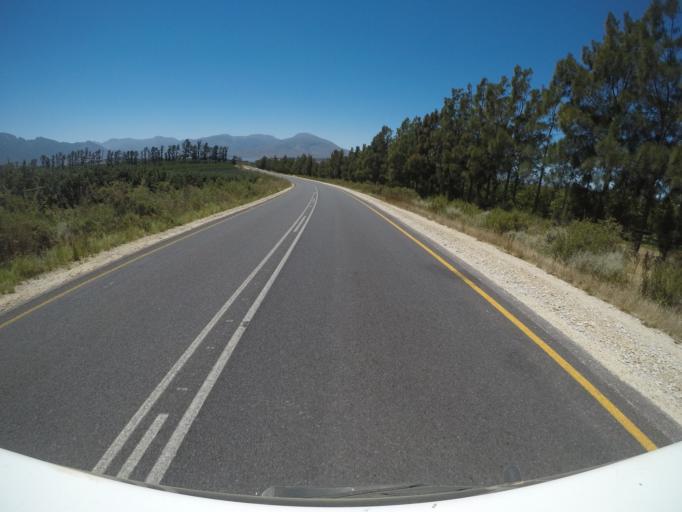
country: ZA
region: Western Cape
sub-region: Overberg District Municipality
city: Grabouw
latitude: -34.0667
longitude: 19.1316
